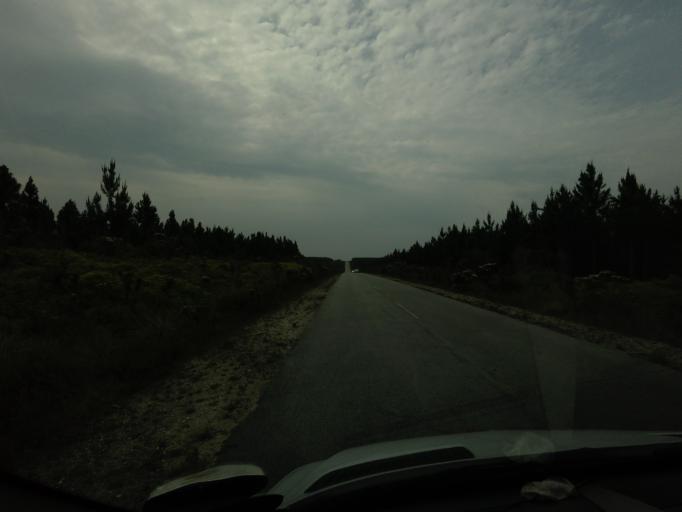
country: ZA
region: Eastern Cape
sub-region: Cacadu District Municipality
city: Kareedouw
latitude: -34.0010
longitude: 23.8579
